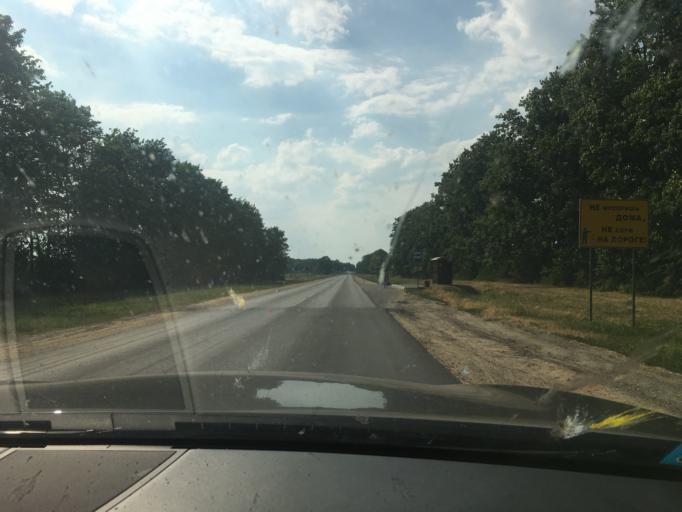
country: BY
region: Brest
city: Pruzhany
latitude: 52.5412
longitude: 24.4473
